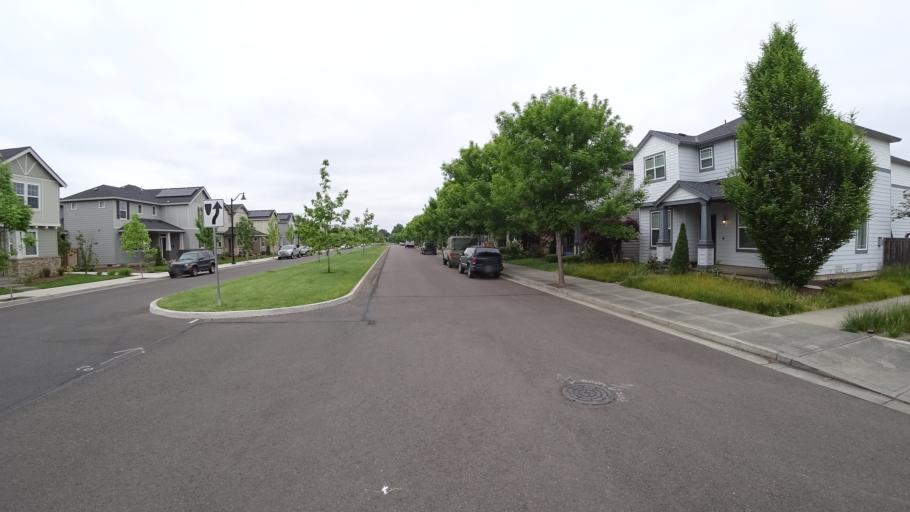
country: US
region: Oregon
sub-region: Washington County
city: Aloha
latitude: 45.4962
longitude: -122.9253
